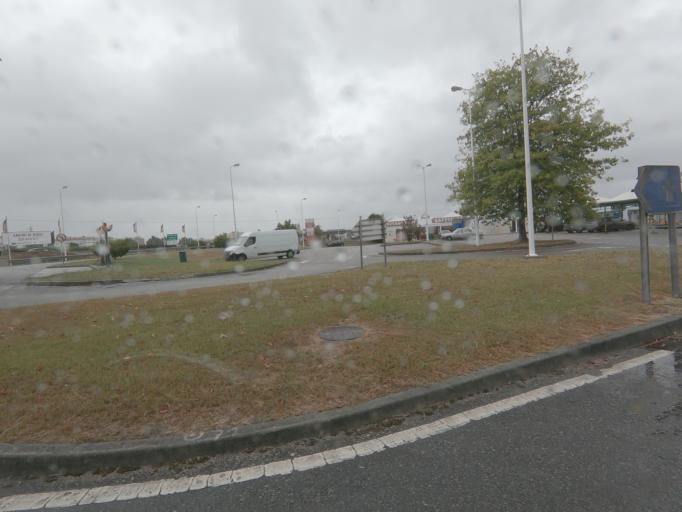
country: PT
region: Porto
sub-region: Maia
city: Pedroucos
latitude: 41.2002
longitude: -8.5662
